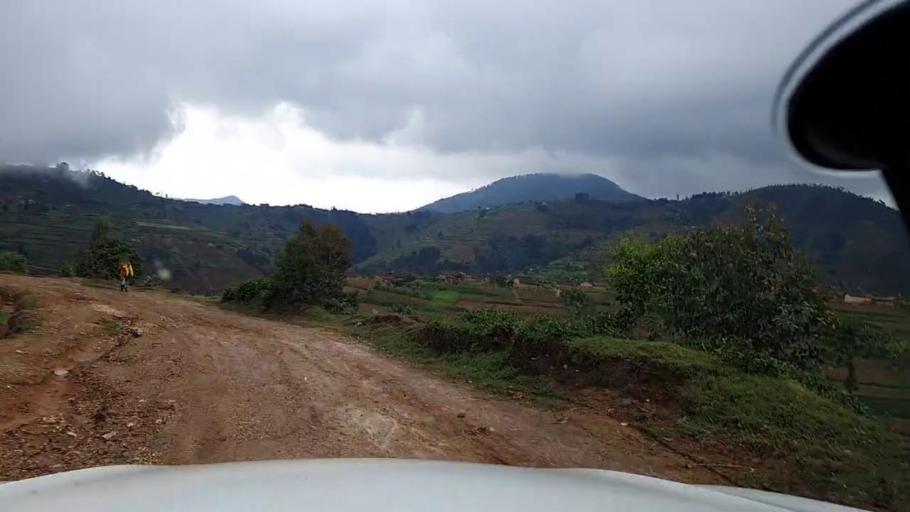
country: RW
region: Western Province
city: Kibuye
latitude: -2.0826
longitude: 29.5070
